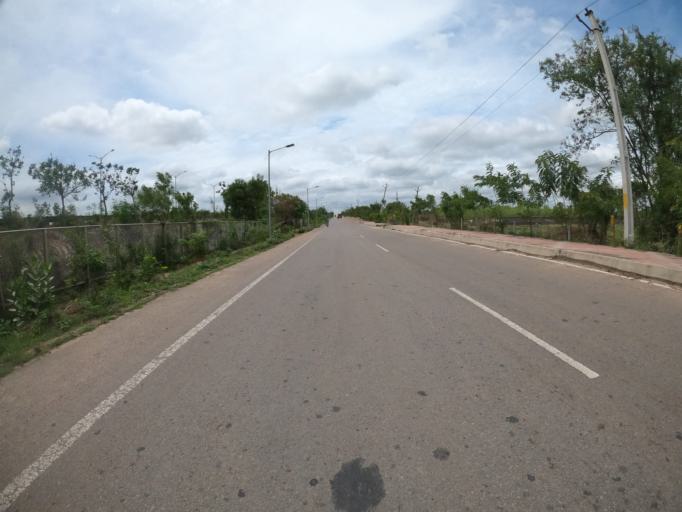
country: IN
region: Telangana
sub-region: Hyderabad
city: Hyderabad
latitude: 17.2932
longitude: 78.3806
